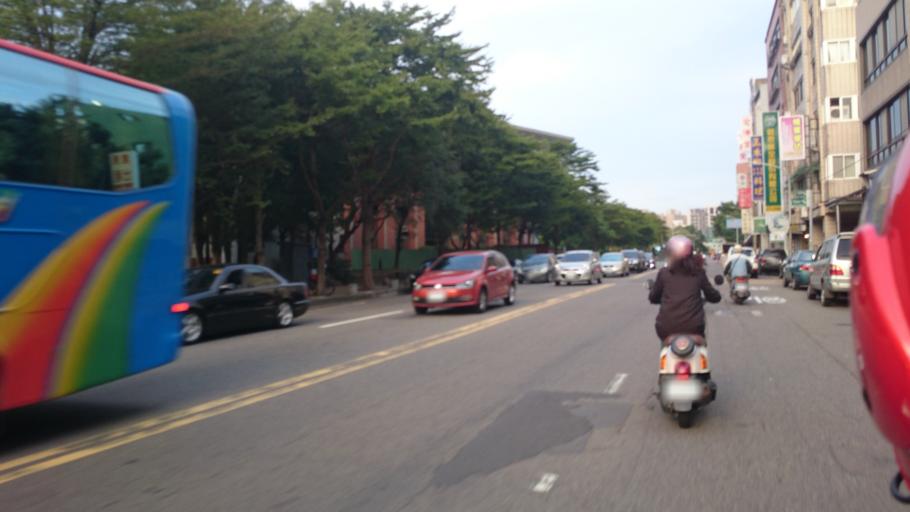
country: TW
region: Taiwan
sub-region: Hsinchu
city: Hsinchu
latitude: 24.7985
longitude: 120.9785
